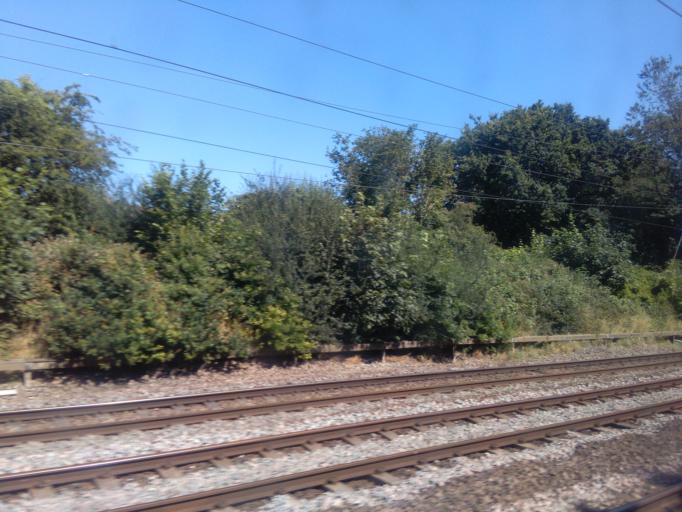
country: GB
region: England
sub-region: Hertfordshire
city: Harpenden
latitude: 51.8028
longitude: -0.3425
